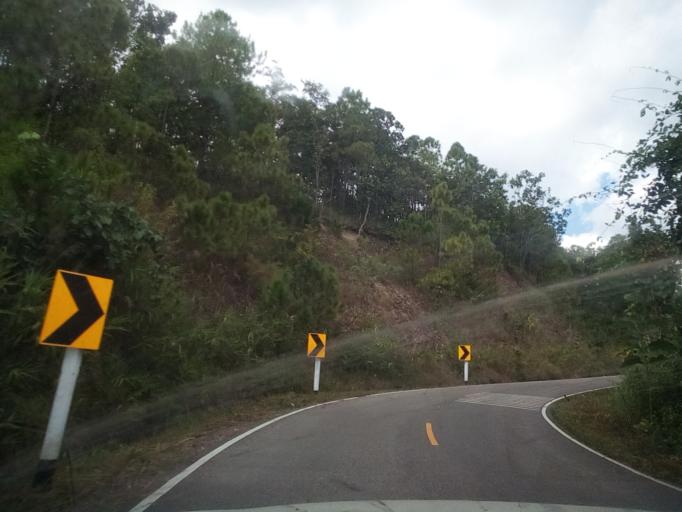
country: TH
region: Chiang Mai
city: Samoeng
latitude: 18.9058
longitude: 98.6754
